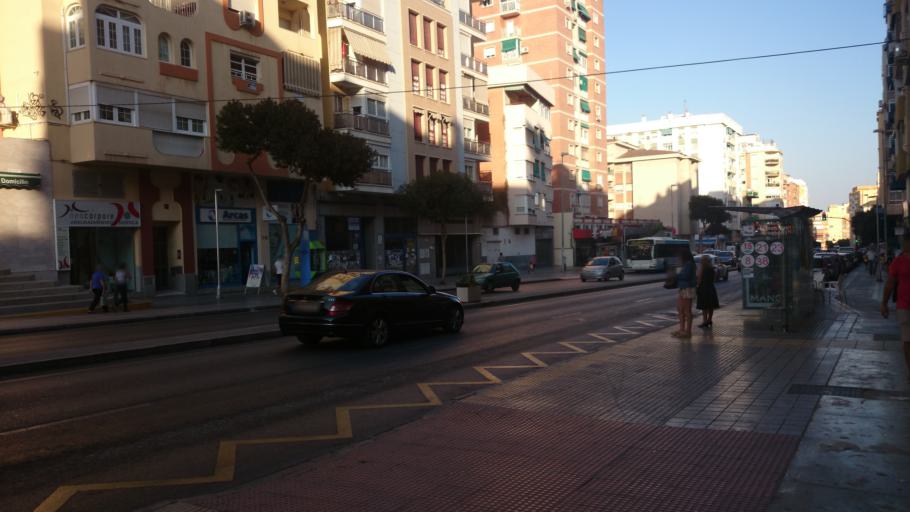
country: ES
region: Andalusia
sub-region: Provincia de Malaga
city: Malaga
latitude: 36.7223
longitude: -4.4473
